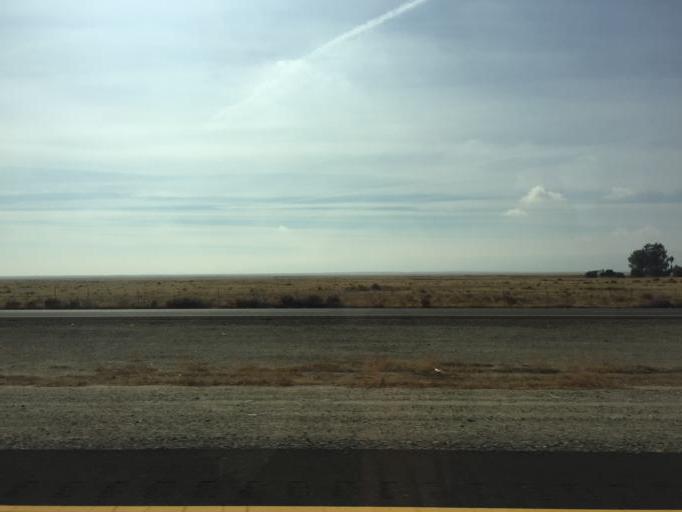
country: US
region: California
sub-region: Kern County
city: Lost Hills
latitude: 35.6153
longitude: -119.8569
